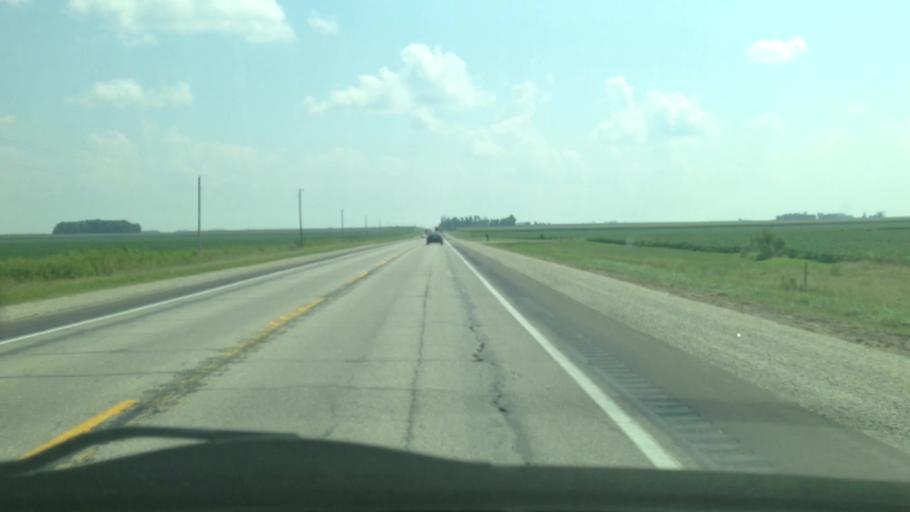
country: US
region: Iowa
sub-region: Howard County
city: Cresco
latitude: 43.4205
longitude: -92.2987
